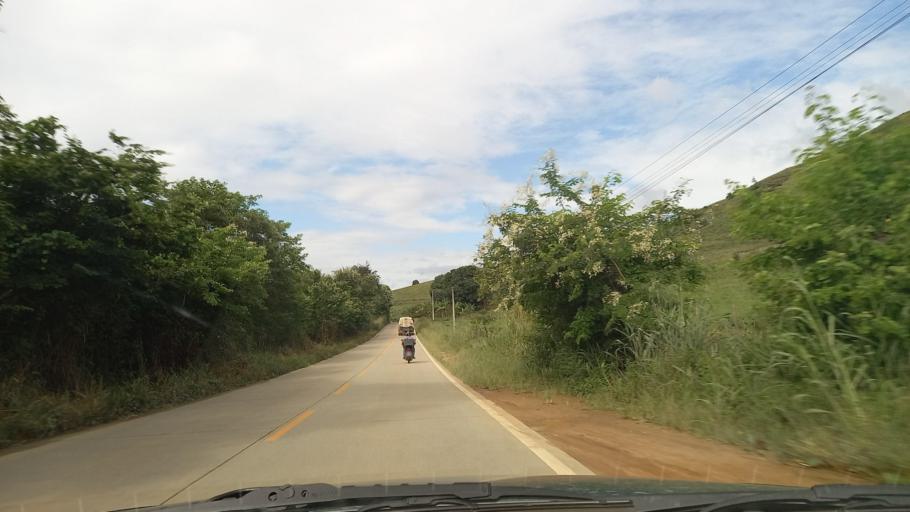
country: BR
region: Pernambuco
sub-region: Maraial
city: Maraial
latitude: -8.7503
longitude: -35.8249
